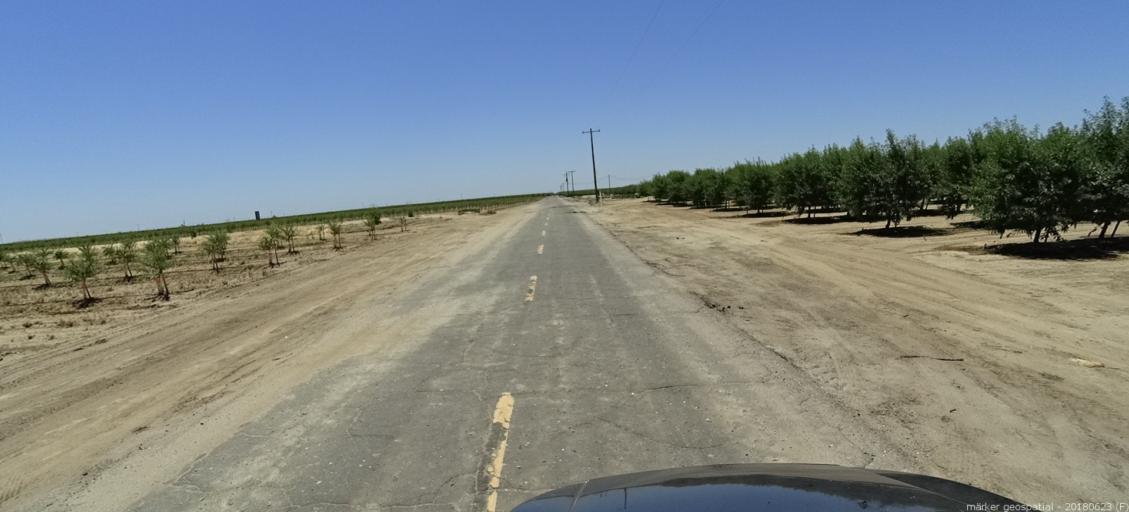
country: US
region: California
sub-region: Madera County
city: Chowchilla
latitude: 37.0970
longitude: -120.2385
